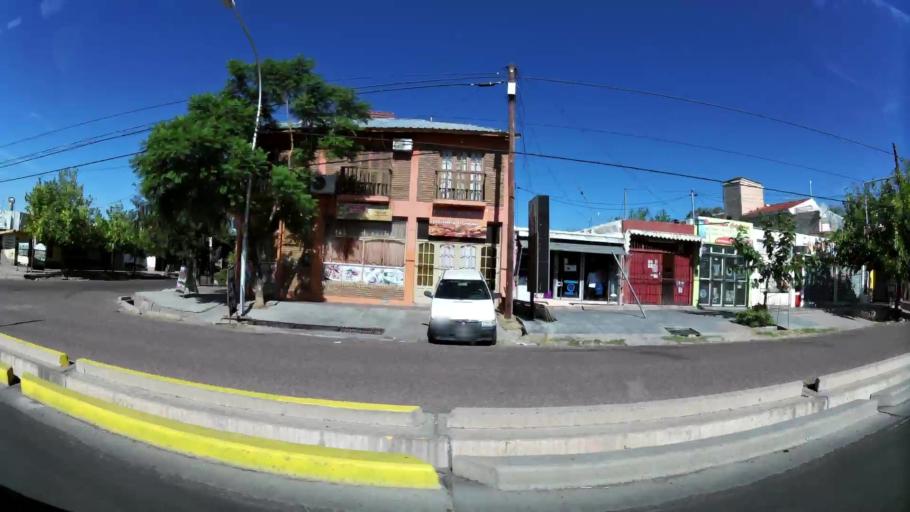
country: AR
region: Mendoza
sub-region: Departamento de Godoy Cruz
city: Godoy Cruz
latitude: -32.9375
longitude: -68.8017
